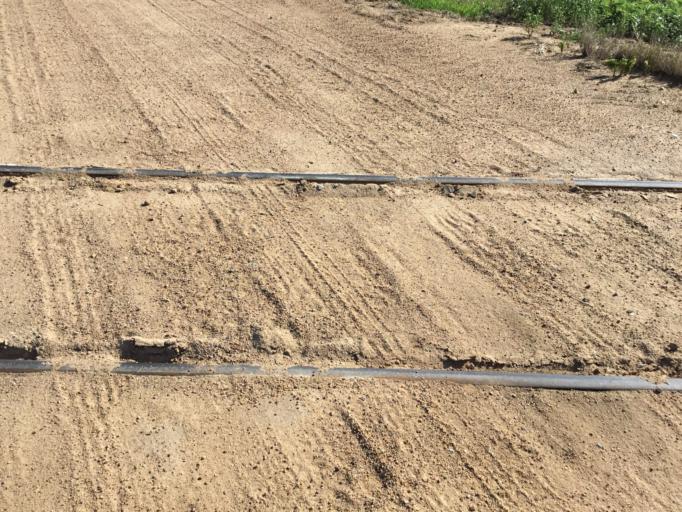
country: US
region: Kansas
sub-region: Kingman County
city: Kingman
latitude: 37.5431
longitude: -98.0268
